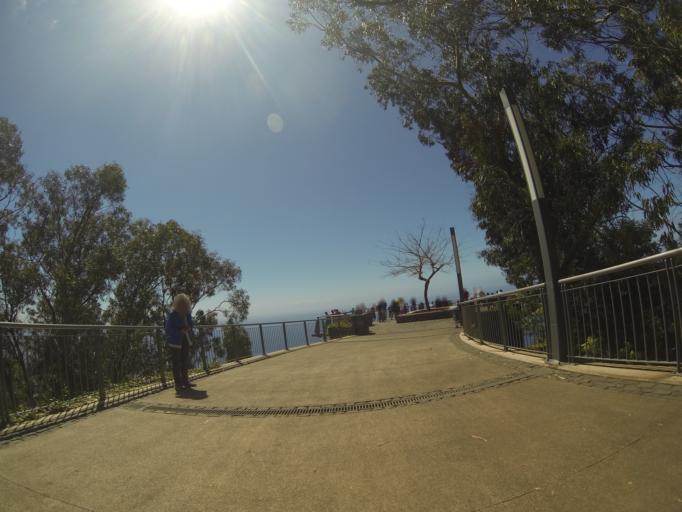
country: PT
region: Madeira
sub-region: Ribeira Brava
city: Campanario
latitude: 32.6567
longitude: -17.0045
